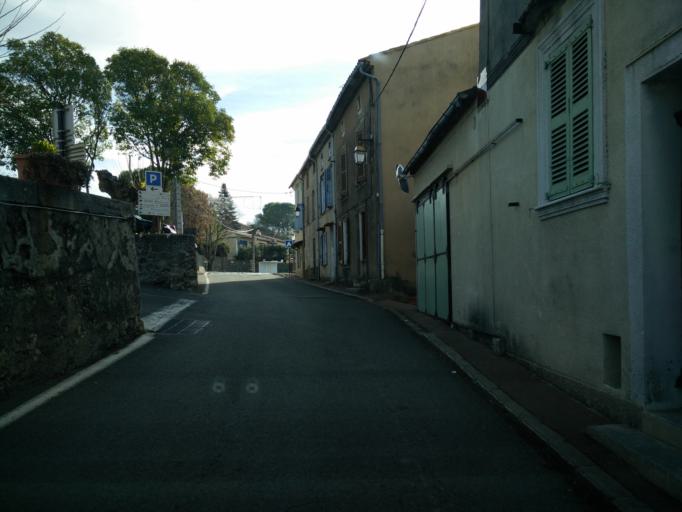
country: FR
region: Provence-Alpes-Cote d'Azur
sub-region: Departement du Var
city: Saint-Paul-en-Foret
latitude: 43.5670
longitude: 6.6920
